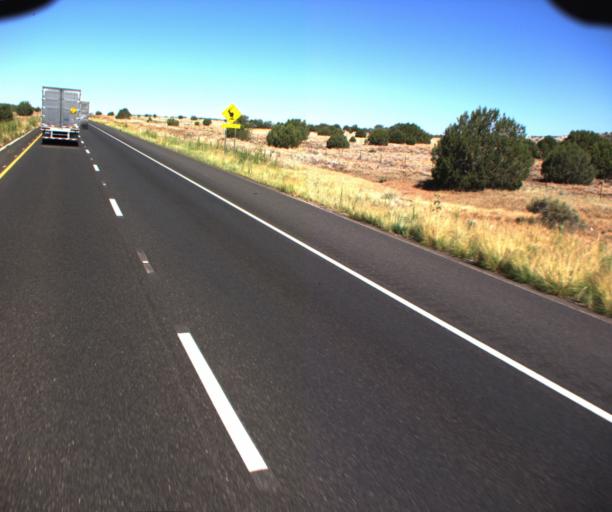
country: US
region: Arizona
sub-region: Yavapai County
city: Paulden
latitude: 35.2496
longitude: -112.6888
